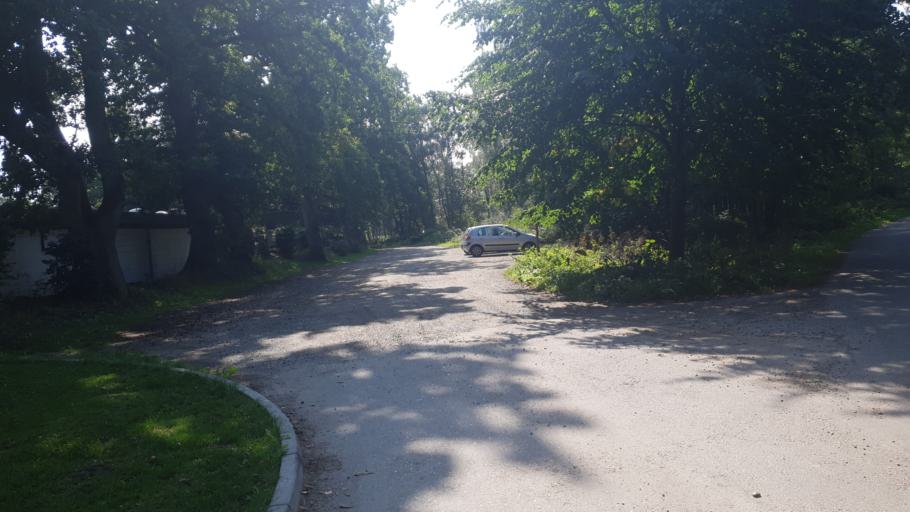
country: DK
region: South Denmark
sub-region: Fredericia Kommune
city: Fredericia
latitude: 55.5541
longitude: 9.7234
